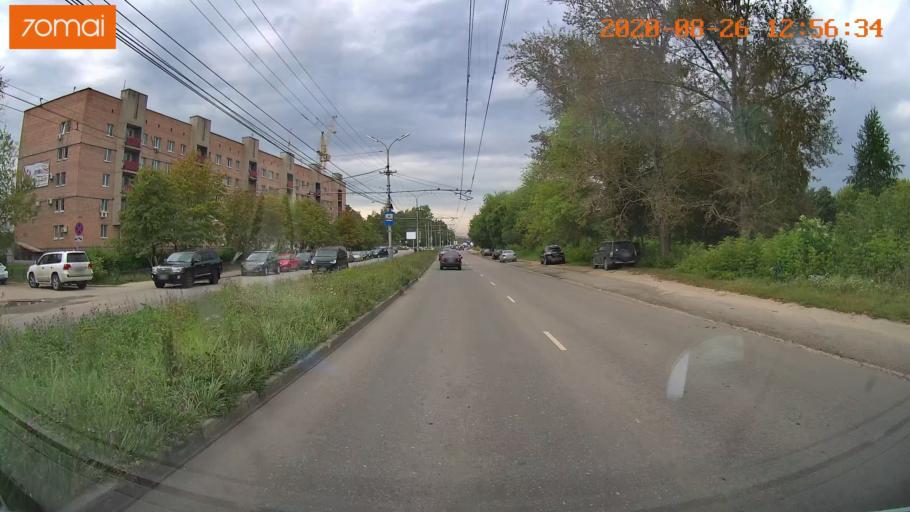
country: RU
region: Rjazan
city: Ryazan'
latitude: 54.6140
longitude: 39.7479
